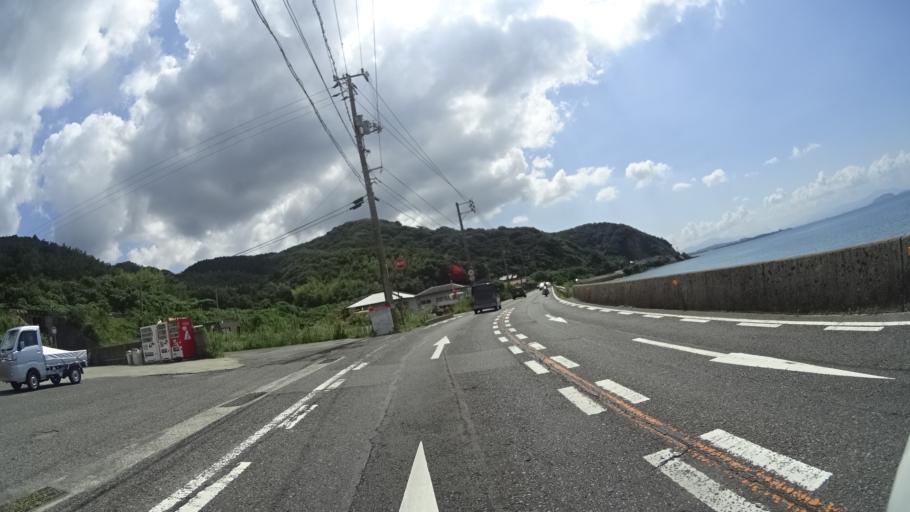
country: JP
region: Yamaguchi
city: Shimonoseki
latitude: 34.0616
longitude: 130.9112
